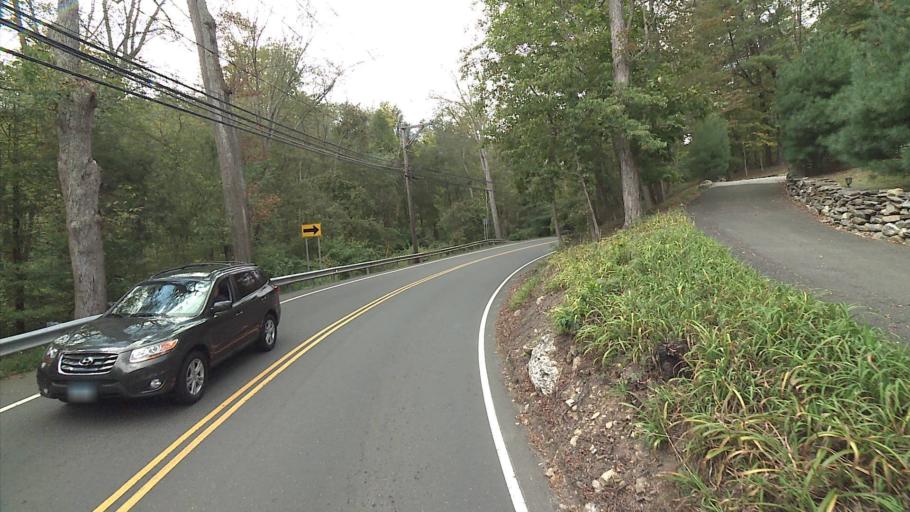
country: US
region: Connecticut
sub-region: Middlesex County
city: Chester Center
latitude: 41.3979
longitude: -72.4662
